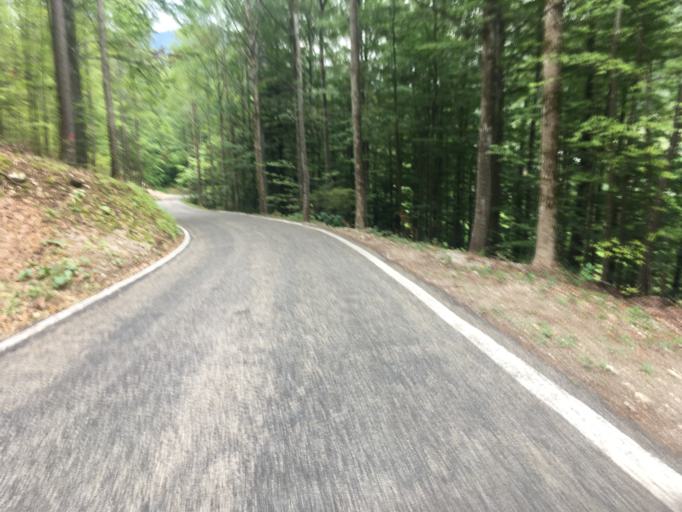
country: CH
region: Solothurn
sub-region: Bezirk Thal
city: Welschenrohr
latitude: 47.2613
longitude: 7.4826
